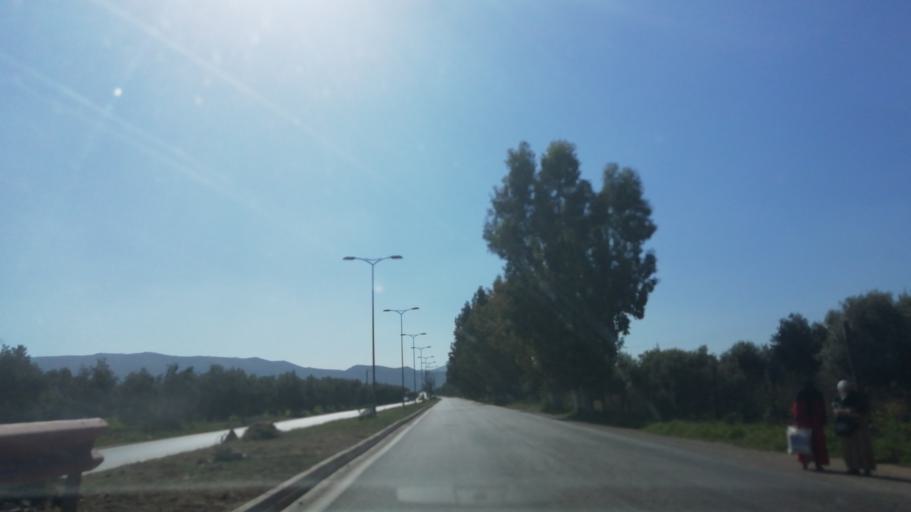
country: DZ
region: Mascara
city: Sig
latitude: 35.5471
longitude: -0.2055
